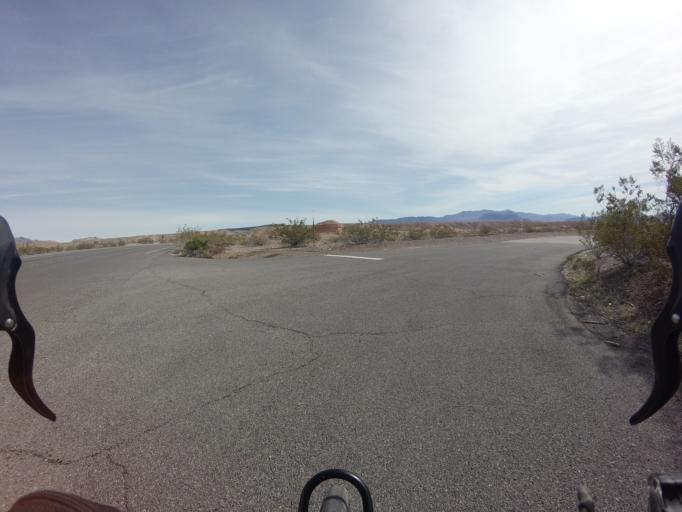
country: US
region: Nevada
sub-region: Clark County
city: Boulder City
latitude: 36.1529
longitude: -114.8338
